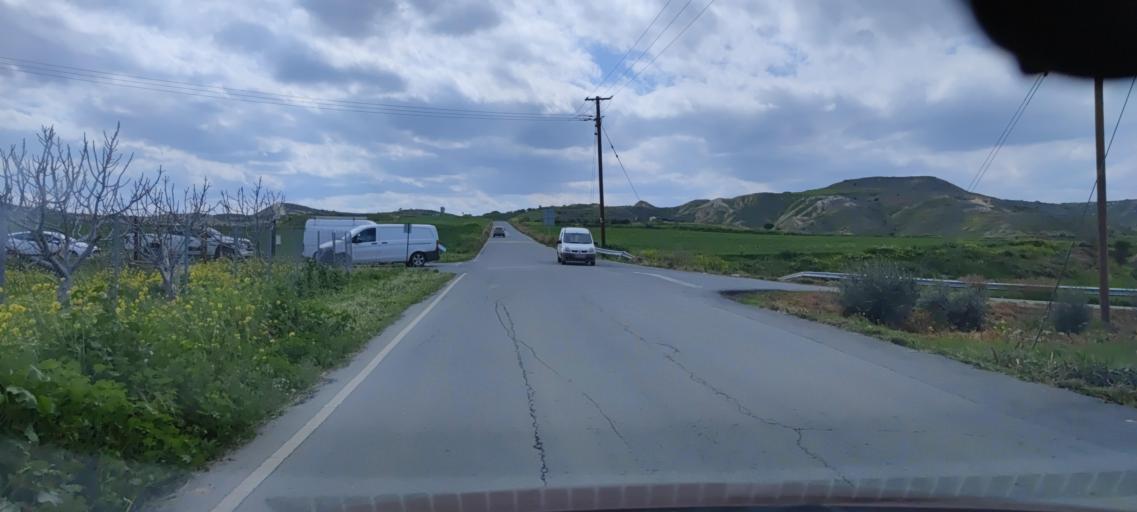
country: CY
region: Lefkosia
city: Tseri
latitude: 35.0386
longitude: 33.3155
